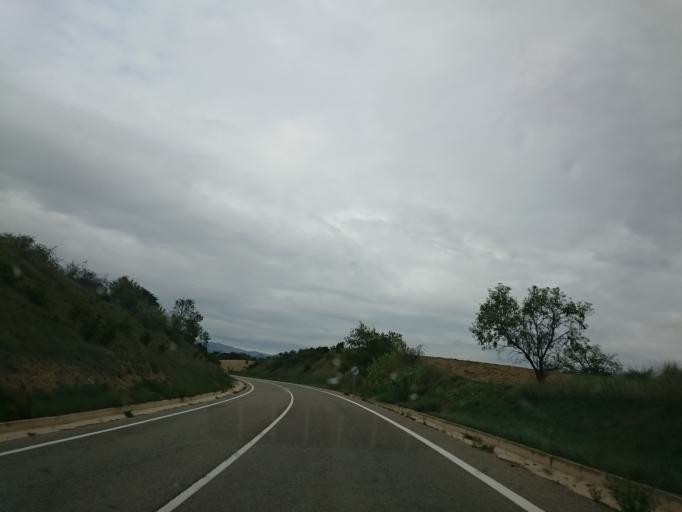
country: ES
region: Catalonia
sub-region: Provincia de Lleida
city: Llimiana
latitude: 42.1086
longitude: 1.0290
